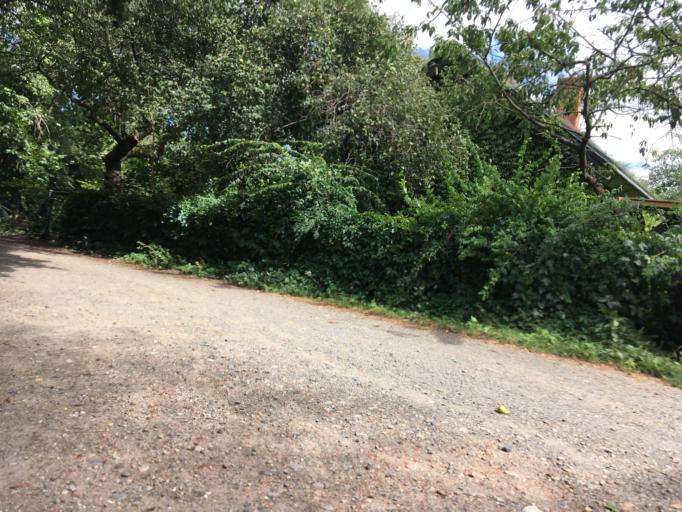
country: DE
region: Berlin
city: Staaken
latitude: 52.5195
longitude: 13.1362
